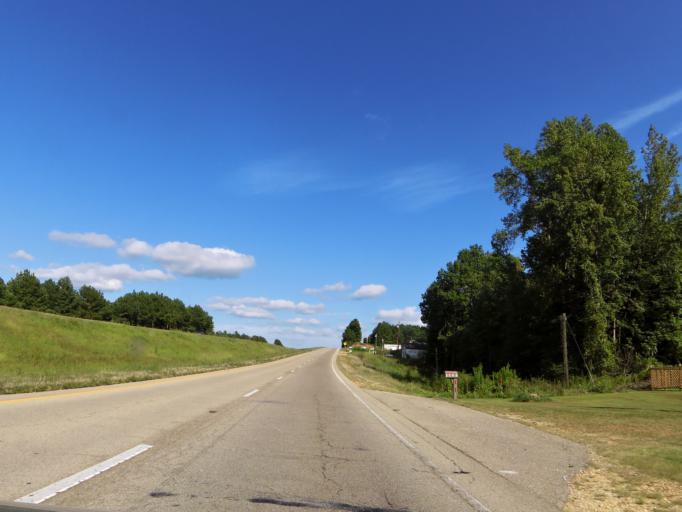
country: US
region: Mississippi
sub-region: Alcorn County
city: Farmington
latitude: 34.8564
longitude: -88.3784
